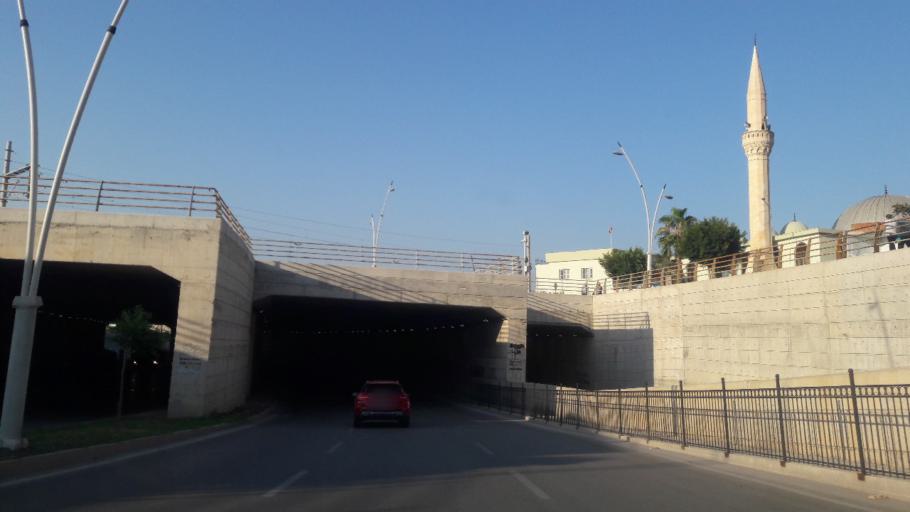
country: TR
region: Adana
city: Seyhan
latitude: 36.9966
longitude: 35.3014
